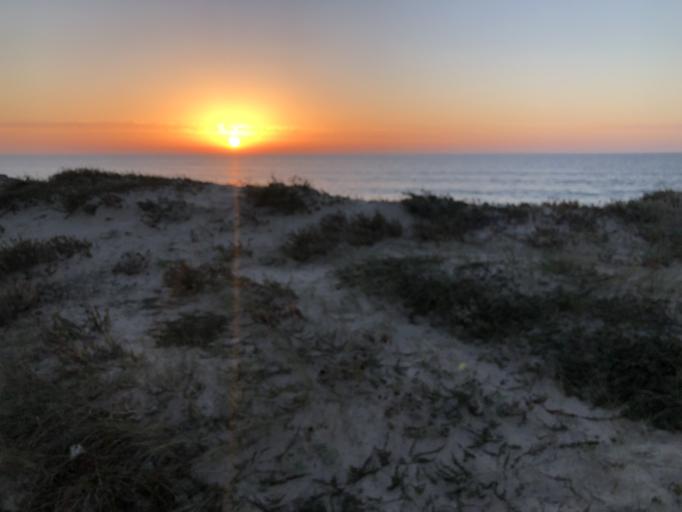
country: PT
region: Porto
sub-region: Vila do Conde
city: Arvore
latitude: 41.3153
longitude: -8.7391
